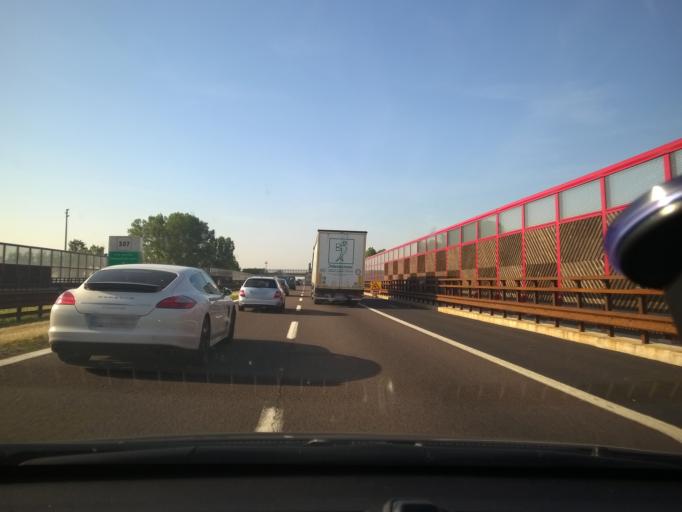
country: IT
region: Emilia-Romagna
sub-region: Provincia di Modena
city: Campogalliano
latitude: 44.7206
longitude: 10.8456
